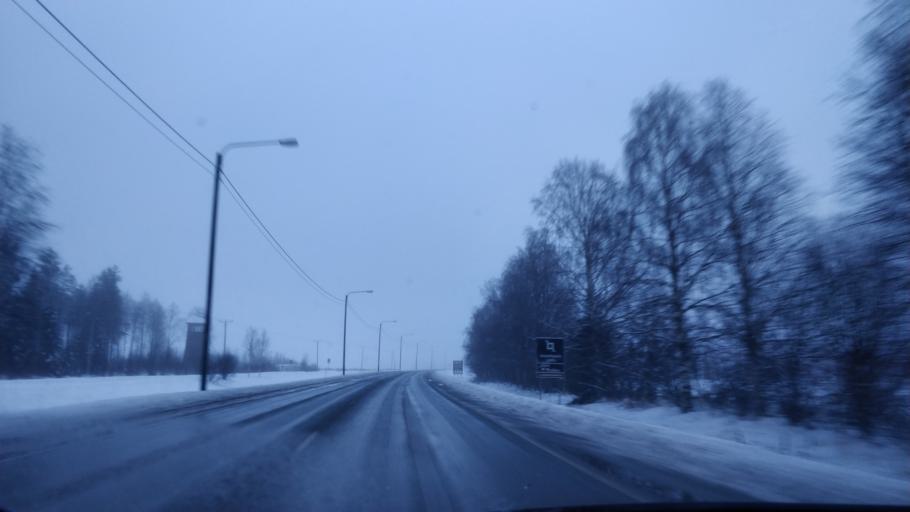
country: FI
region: Lapland
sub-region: Kemi-Tornio
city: Tervola
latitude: 66.1503
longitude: 24.9791
